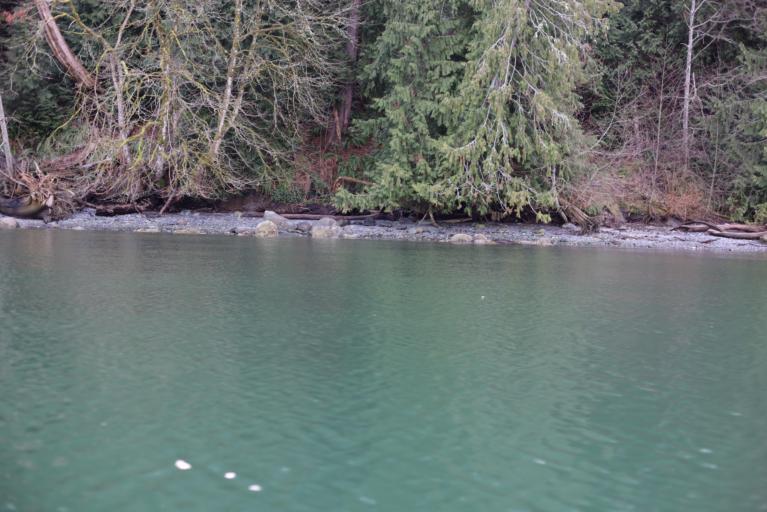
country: CA
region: British Columbia
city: Duncan
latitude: 48.7408
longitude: -123.6114
